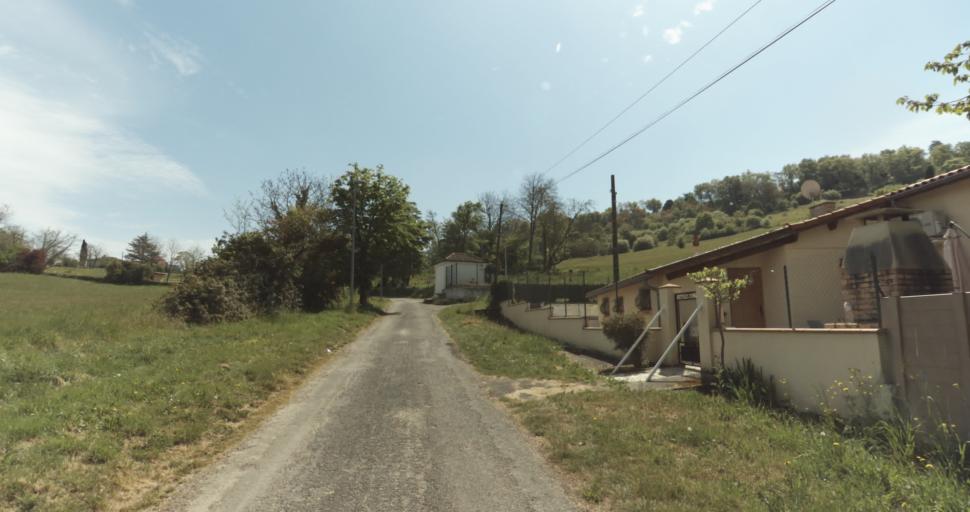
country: FR
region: Aquitaine
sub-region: Departement du Lot-et-Garonne
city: Agen
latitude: 44.2123
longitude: 0.6522
